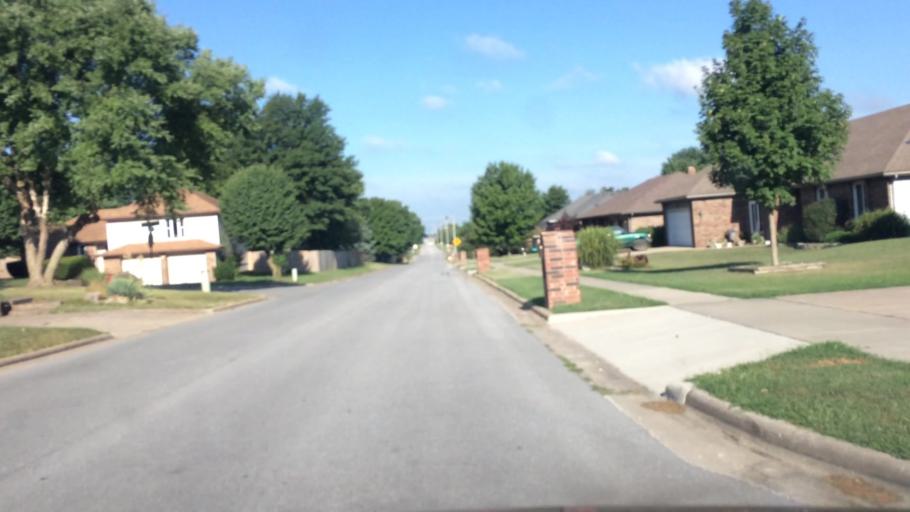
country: US
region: Missouri
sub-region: Greene County
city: Springfield
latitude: 37.2661
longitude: -93.2687
